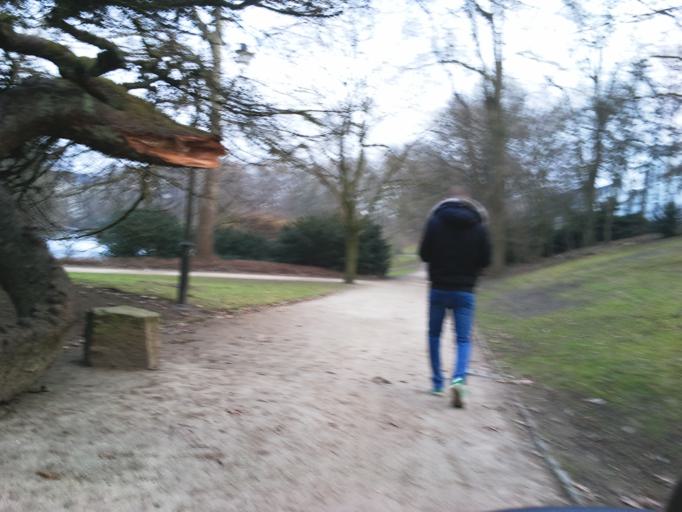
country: DE
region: Bremen
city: Bremen
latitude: 53.0820
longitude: 8.7994
